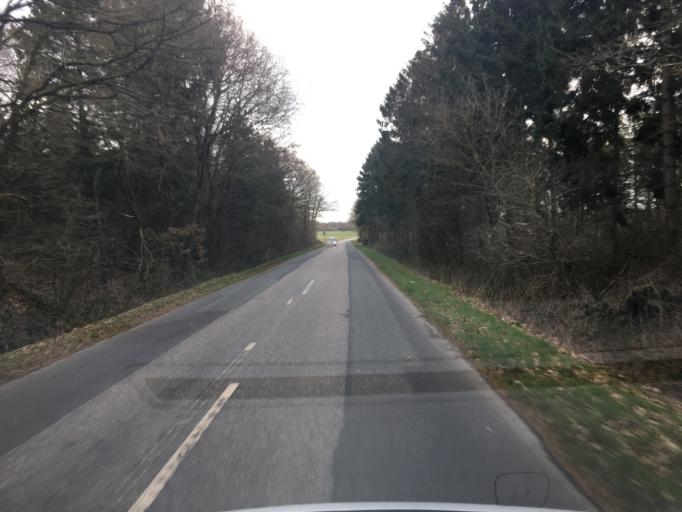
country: DK
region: South Denmark
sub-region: Aabenraa Kommune
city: Krusa
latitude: 54.8977
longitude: 9.4757
